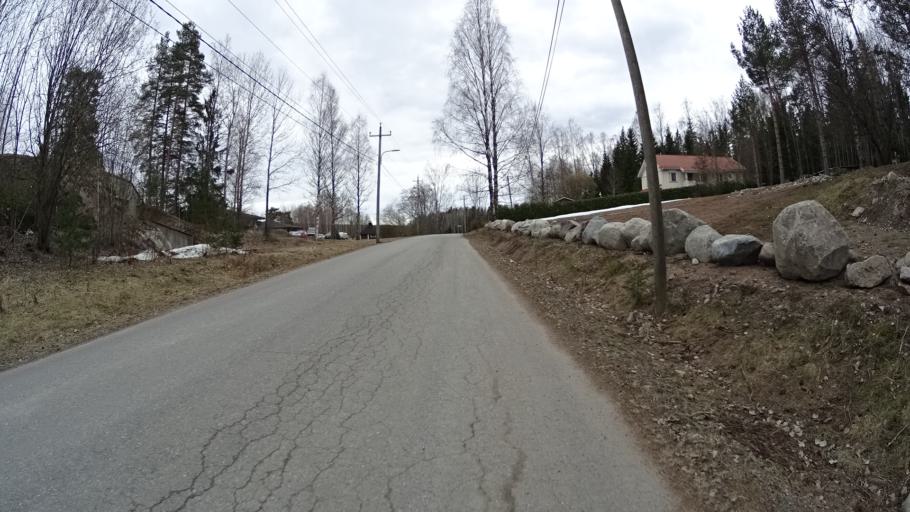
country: FI
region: Uusimaa
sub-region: Helsinki
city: Kilo
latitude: 60.2961
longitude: 24.7859
